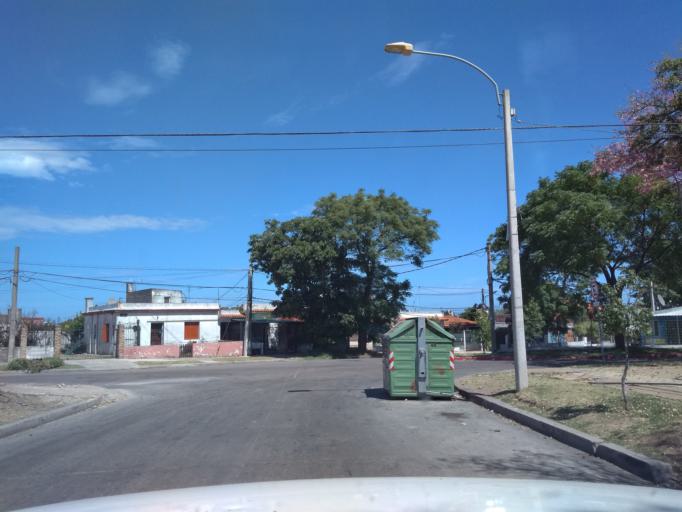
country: UY
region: Montevideo
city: Montevideo
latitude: -34.8886
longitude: -56.1213
